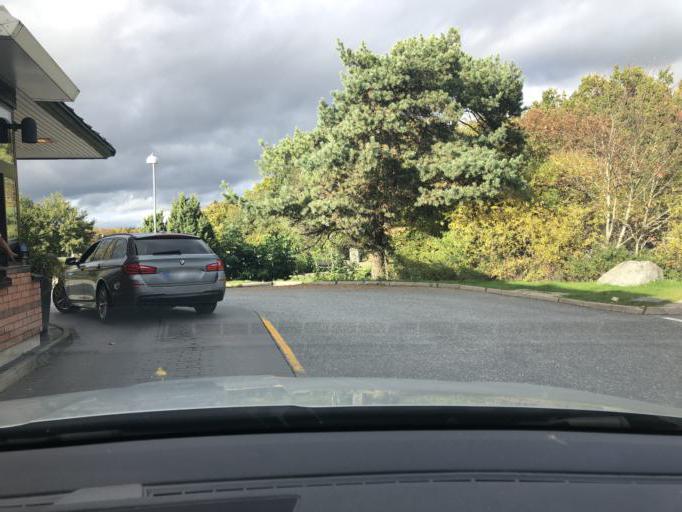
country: SE
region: Stockholm
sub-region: Upplands Vasby Kommun
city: Upplands Vaesby
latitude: 59.5513
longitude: 17.9016
